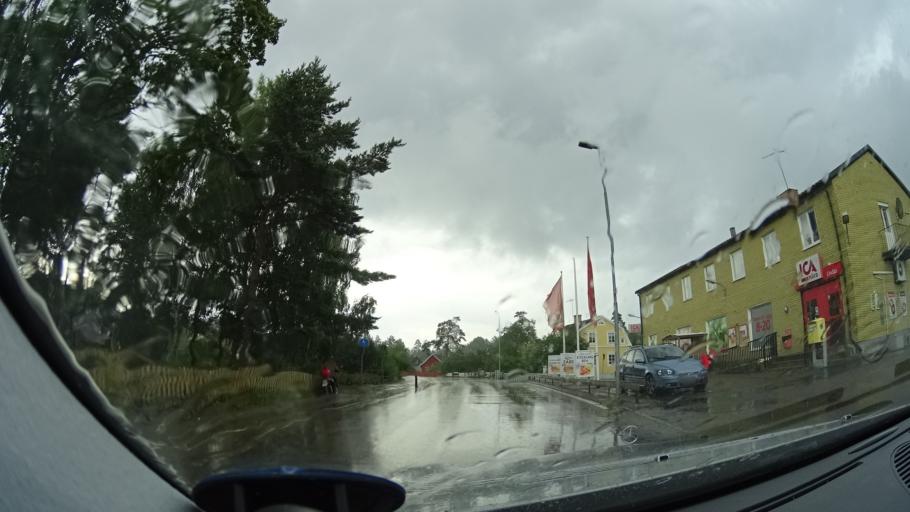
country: SE
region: Kalmar
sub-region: Emmaboda Kommun
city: Emmaboda
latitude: 56.6193
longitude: 15.5681
